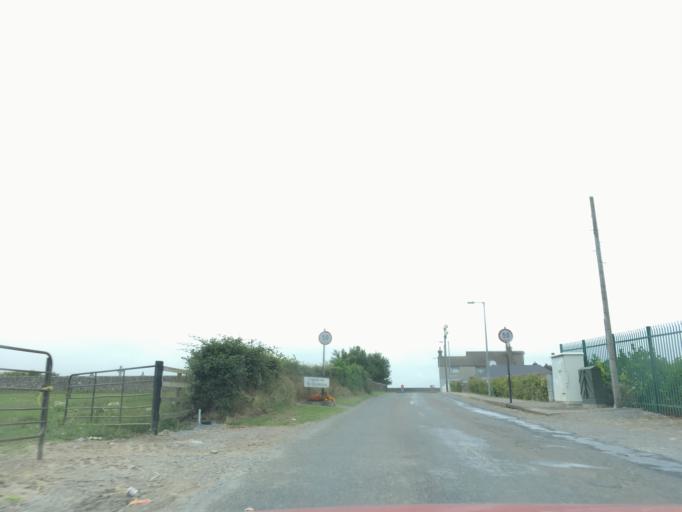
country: IE
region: Munster
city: Cashel
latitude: 52.4691
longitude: -7.8357
